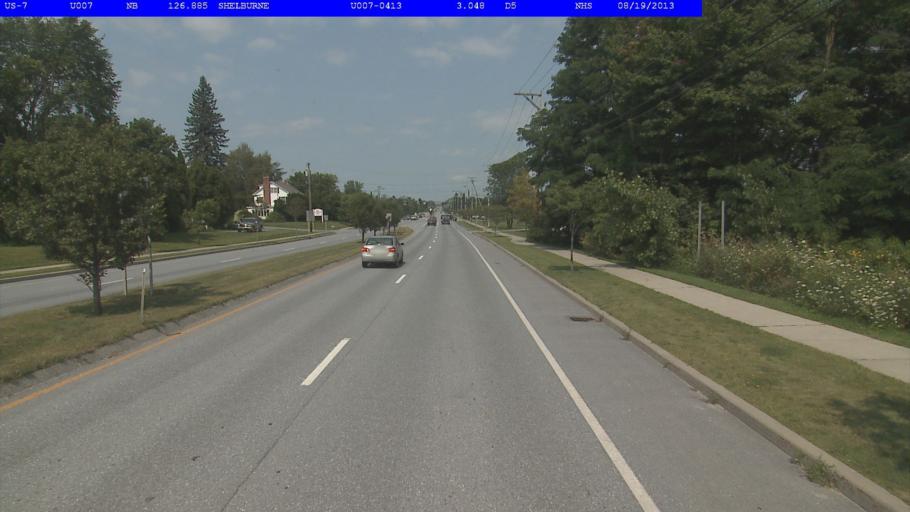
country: US
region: Vermont
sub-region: Chittenden County
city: Burlington
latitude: 44.3944
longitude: -73.2203
